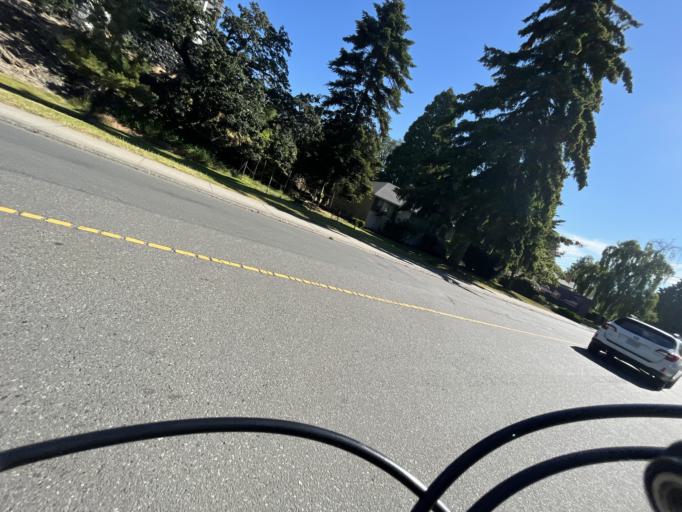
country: CA
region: British Columbia
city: Oak Bay
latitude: 48.4202
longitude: -123.3223
